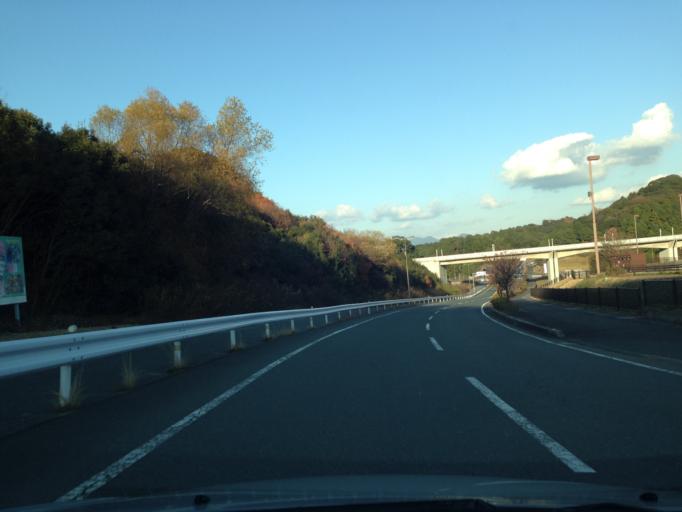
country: JP
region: Shizuoka
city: Fukuroi
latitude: 34.7440
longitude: 137.9636
